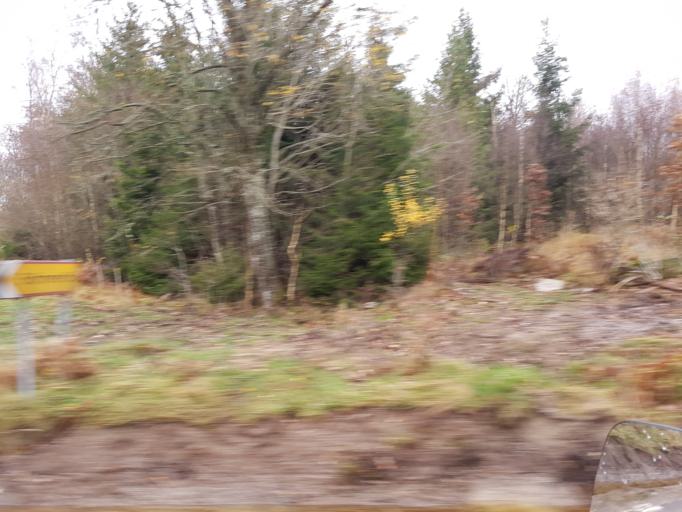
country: SE
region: Vaestra Goetaland
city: Svanesund
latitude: 58.1855
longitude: 11.7760
